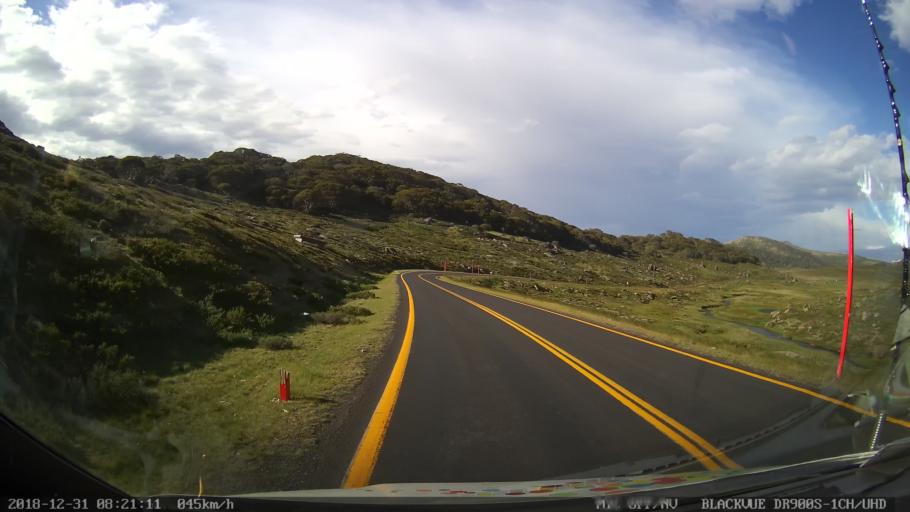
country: AU
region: New South Wales
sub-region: Snowy River
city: Jindabyne
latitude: -36.4266
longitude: 148.3697
